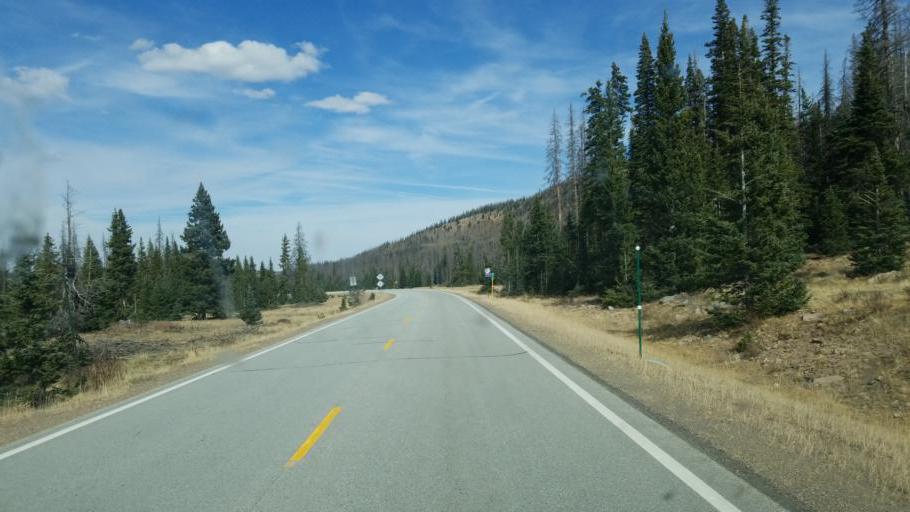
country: US
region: New Mexico
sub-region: Rio Arriba County
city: Chama
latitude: 37.0864
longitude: -106.3801
